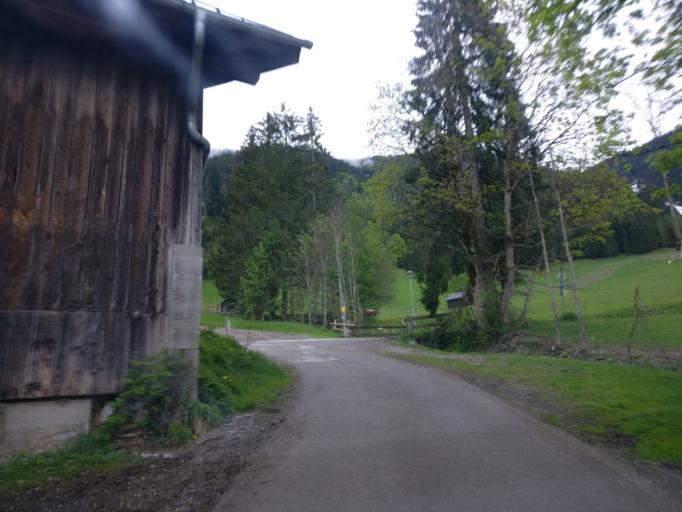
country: AT
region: Salzburg
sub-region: Politischer Bezirk Sankt Johann im Pongau
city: Werfenweng
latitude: 47.4572
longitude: 13.2772
